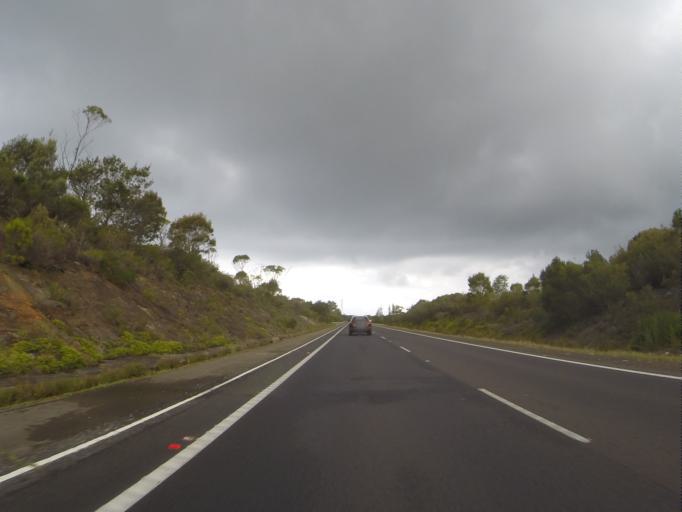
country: AU
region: New South Wales
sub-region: Wollongong
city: Bulli
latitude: -34.2732
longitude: 150.9275
